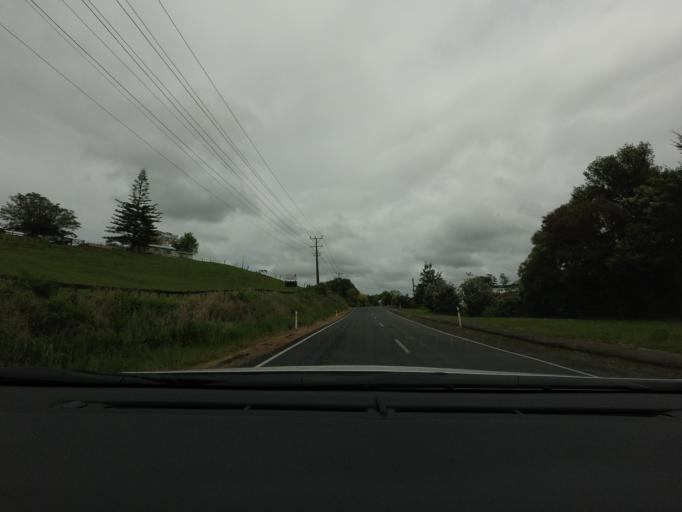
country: NZ
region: Auckland
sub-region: Auckland
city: Waitakere
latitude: -36.8959
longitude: 174.6026
